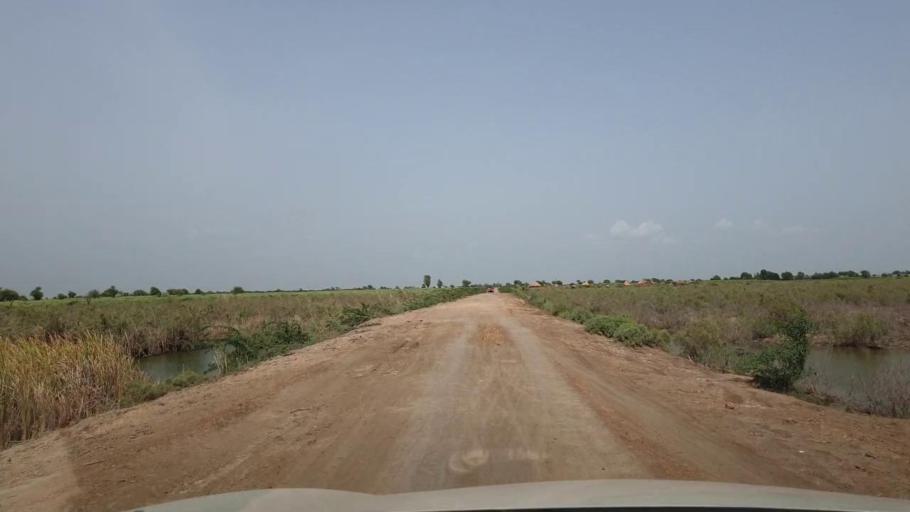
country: PK
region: Sindh
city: Mirwah Gorchani
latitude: 25.2560
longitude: 68.9591
